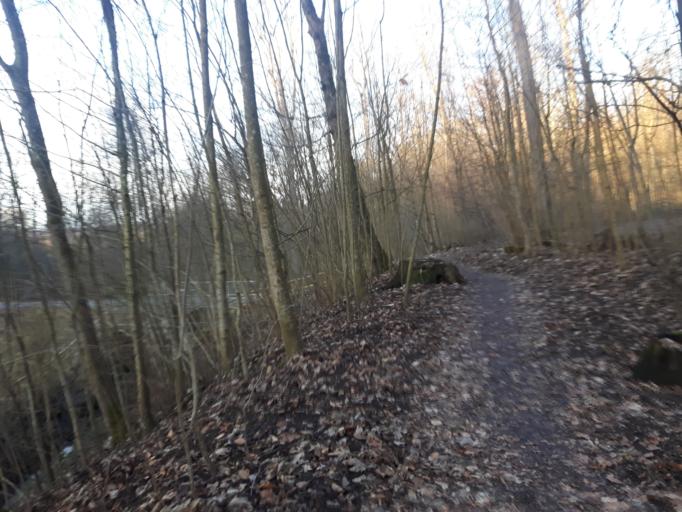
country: DE
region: Baden-Wuerttemberg
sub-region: Regierungsbezirk Stuttgart
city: Heilbronn
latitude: 49.1273
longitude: 9.2558
